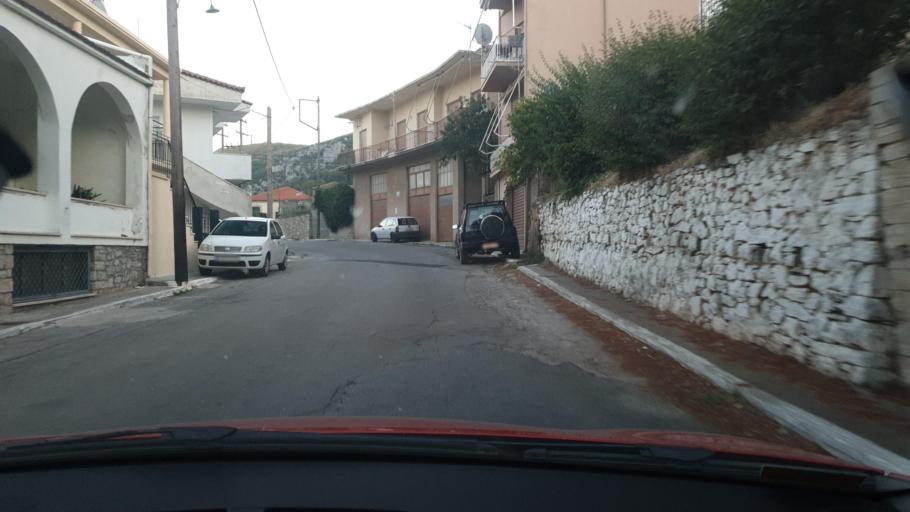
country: GR
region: Central Greece
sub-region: Nomos Evvoias
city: Kymi
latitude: 38.6318
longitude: 24.1048
